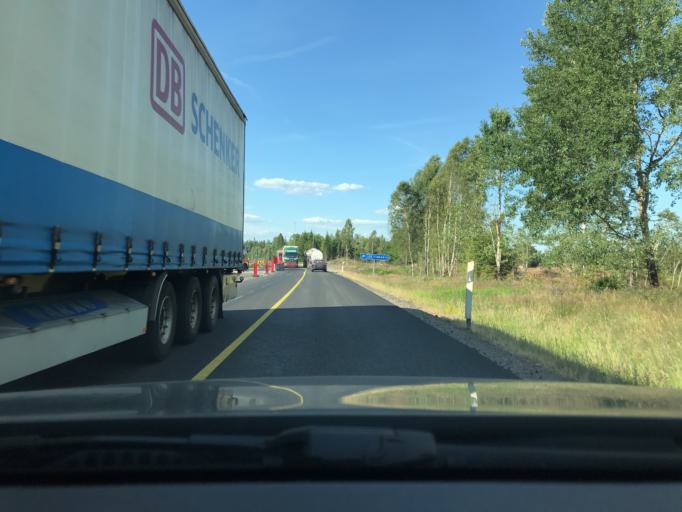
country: SE
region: Kronoberg
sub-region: Almhults Kommun
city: AElmhult
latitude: 56.5600
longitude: 14.1809
